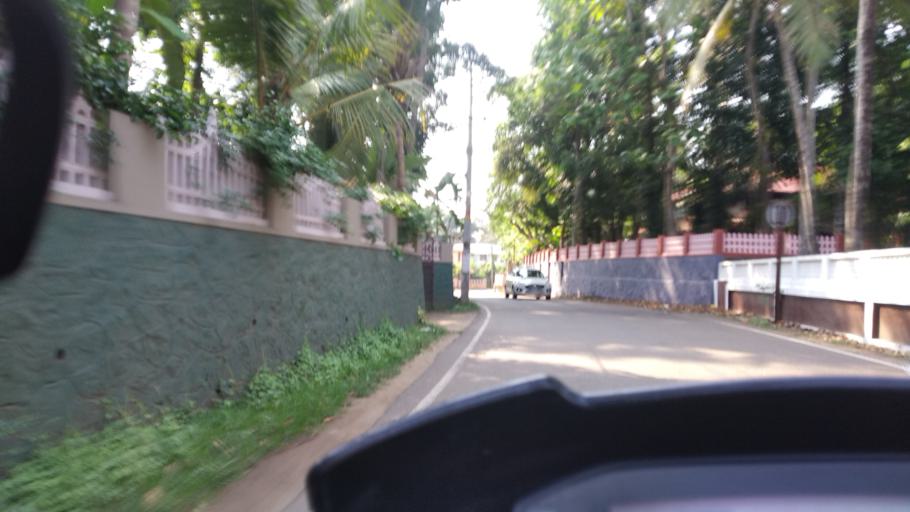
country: IN
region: Kerala
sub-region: Ernakulam
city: Piravam
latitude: 9.8714
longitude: 76.4982
